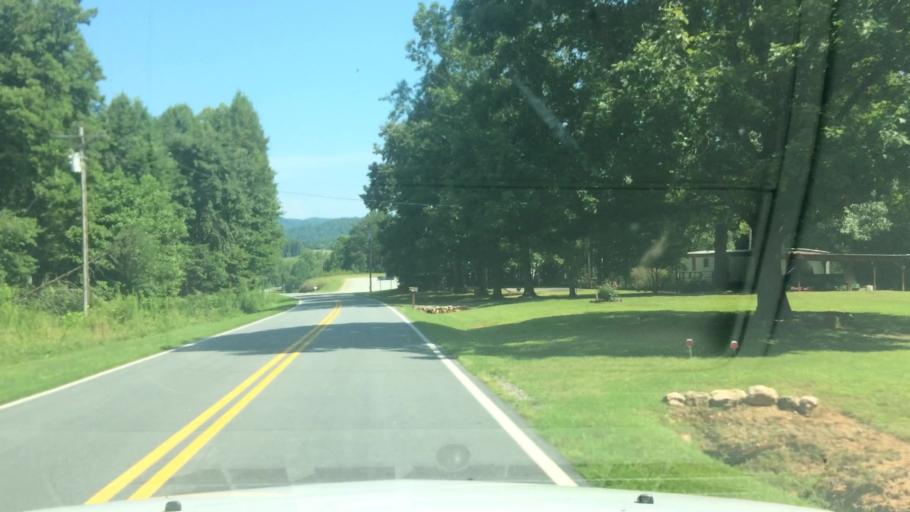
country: US
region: North Carolina
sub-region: Alexander County
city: Taylorsville
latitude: 35.9539
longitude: -81.2678
